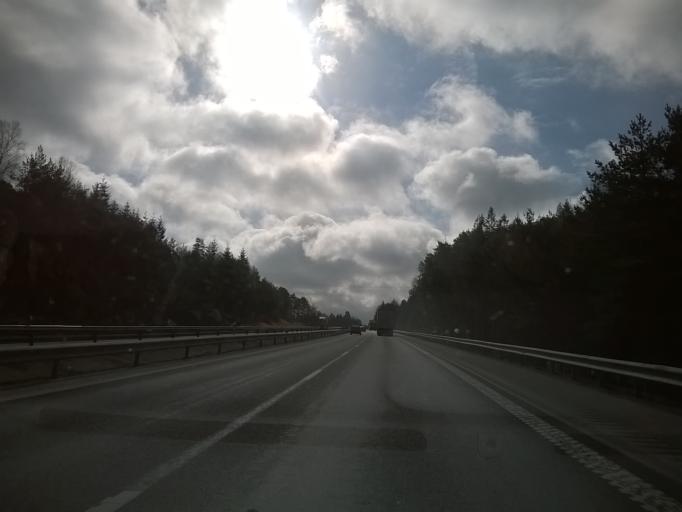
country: SE
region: Halland
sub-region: Kungsbacka Kommun
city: Fjaeras kyrkby
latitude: 57.4047
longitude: 12.1791
